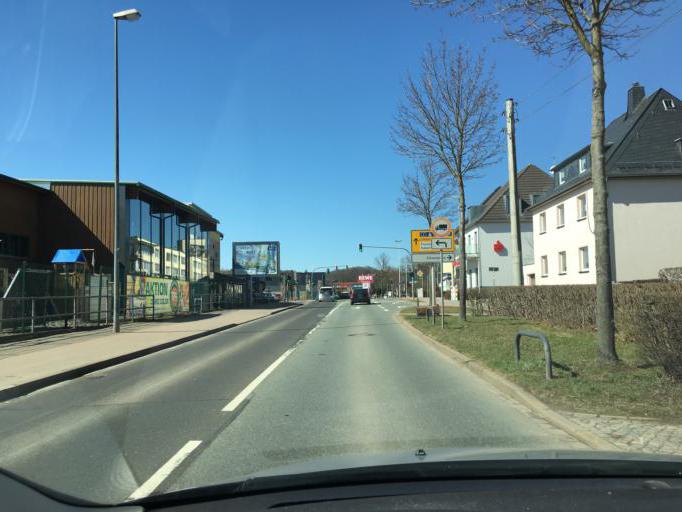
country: DE
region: Saxony
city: Neukirchen
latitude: 50.8248
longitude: 12.8339
